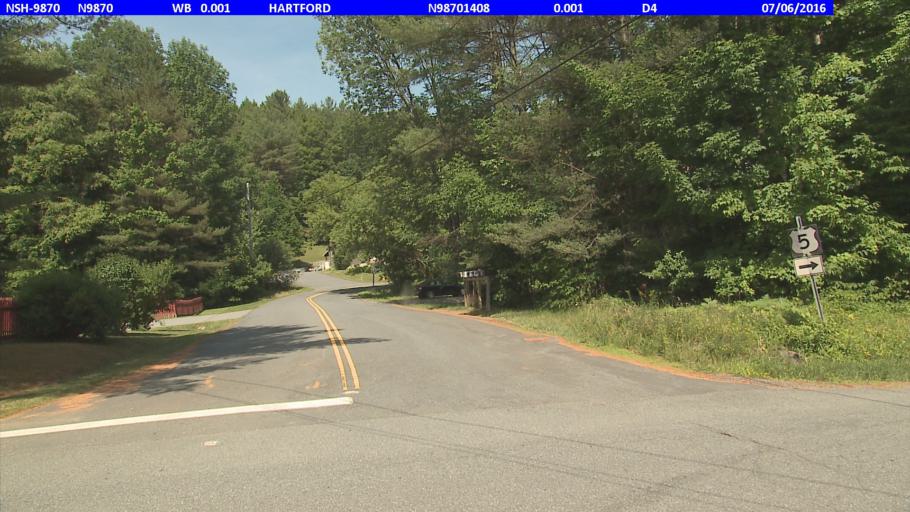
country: US
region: Vermont
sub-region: Windsor County
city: Wilder
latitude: 43.6689
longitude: -72.3256
